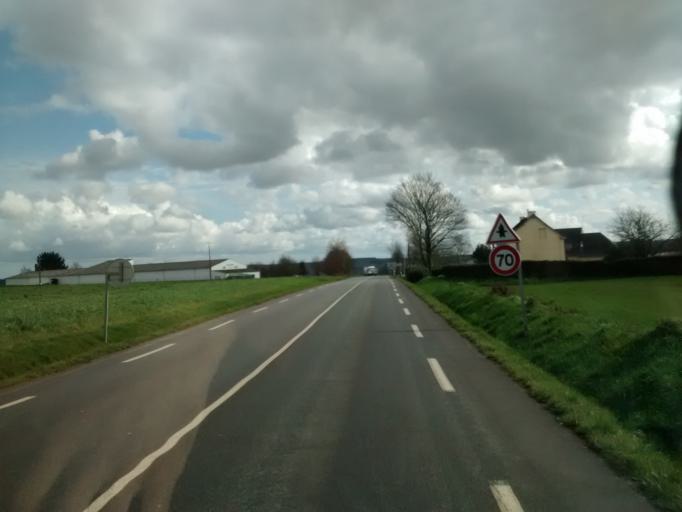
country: FR
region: Brittany
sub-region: Departement du Morbihan
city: Malestroit
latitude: 47.8556
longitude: -2.4222
